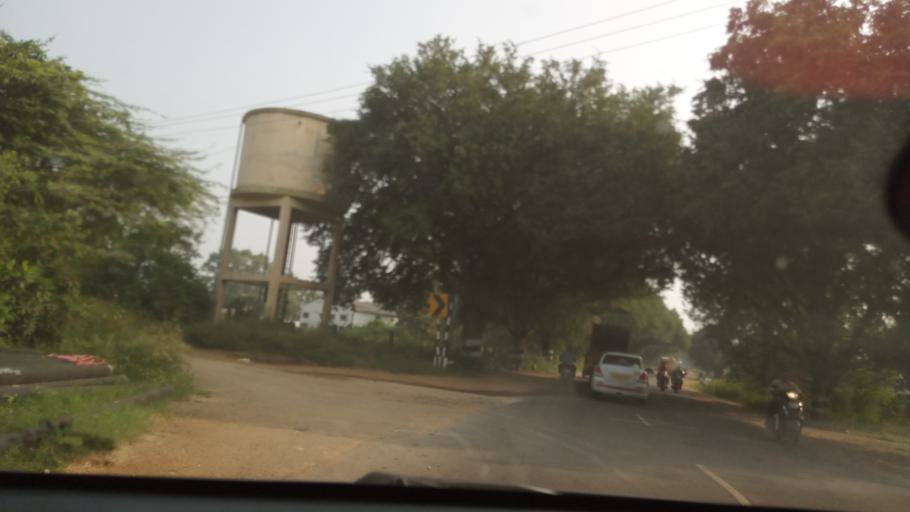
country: IN
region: Tamil Nadu
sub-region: Coimbatore
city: Annur
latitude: 11.1963
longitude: 77.0701
